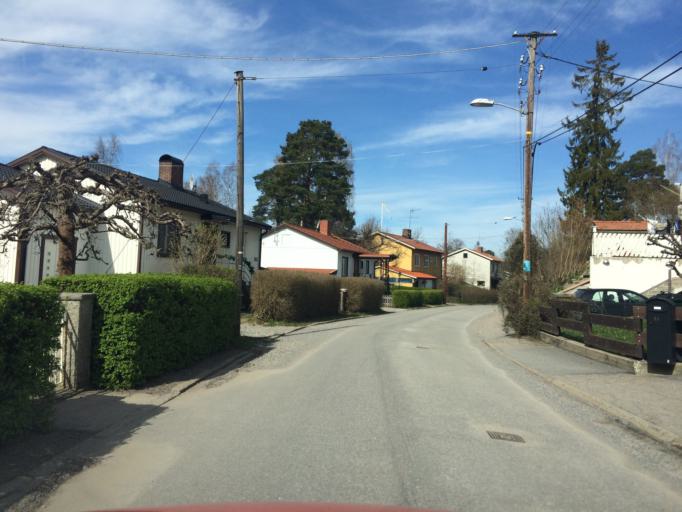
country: SE
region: Stockholm
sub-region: Huddinge Kommun
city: Huddinge
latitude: 59.2821
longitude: 17.9821
